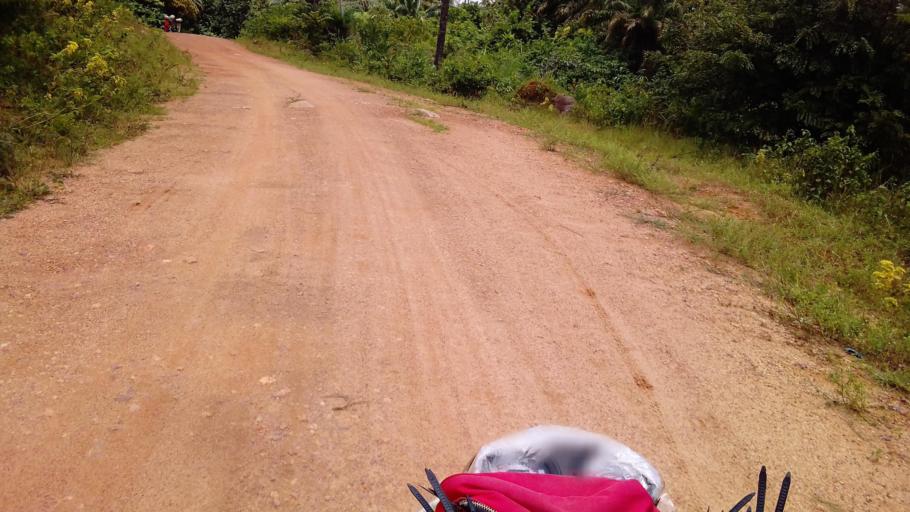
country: SL
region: Eastern Province
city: Koidu
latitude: 8.6940
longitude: -10.9236
